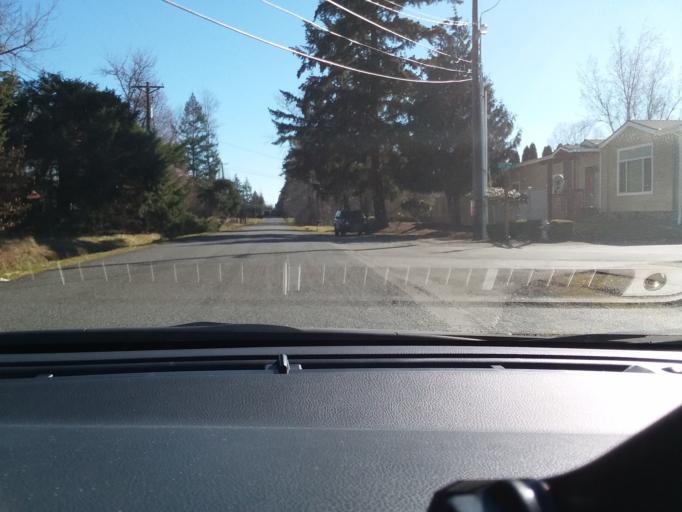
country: US
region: Washington
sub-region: Pierce County
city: Midland
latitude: 47.1725
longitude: -122.4013
